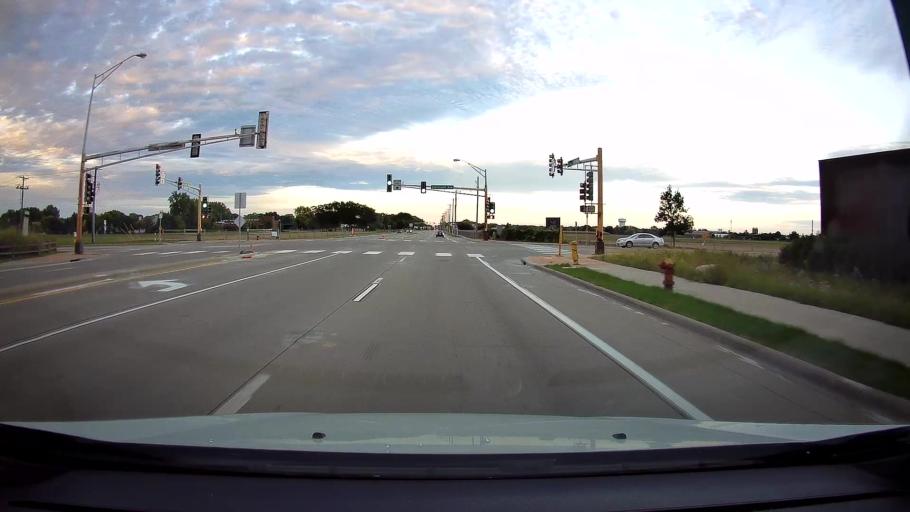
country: US
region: Minnesota
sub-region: Ramsey County
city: Lauderdale
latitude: 44.9916
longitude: -93.1878
